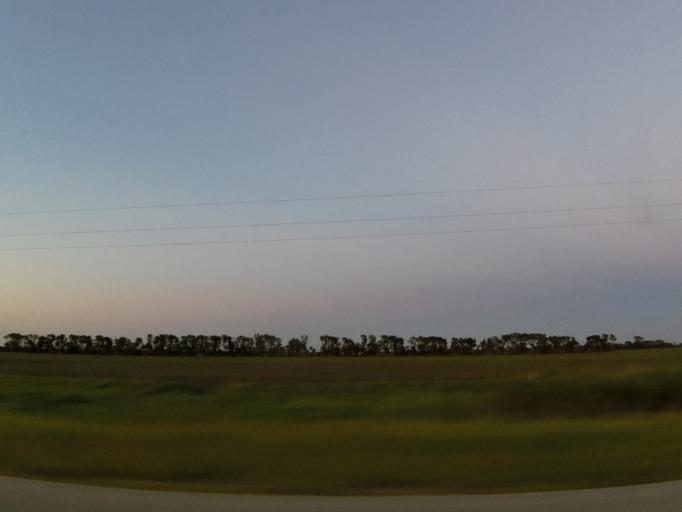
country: US
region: North Dakota
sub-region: Walsh County
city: Grafton
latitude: 48.4067
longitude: -97.1901
